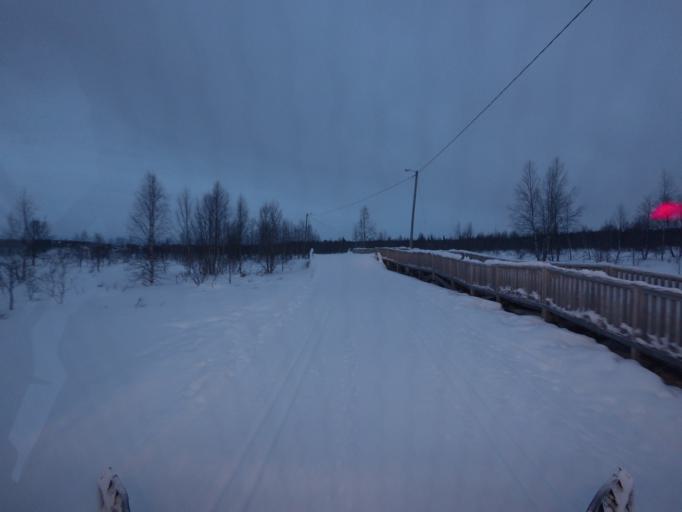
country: FI
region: Lapland
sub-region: Tunturi-Lappi
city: Kolari
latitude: 67.6133
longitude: 24.1682
